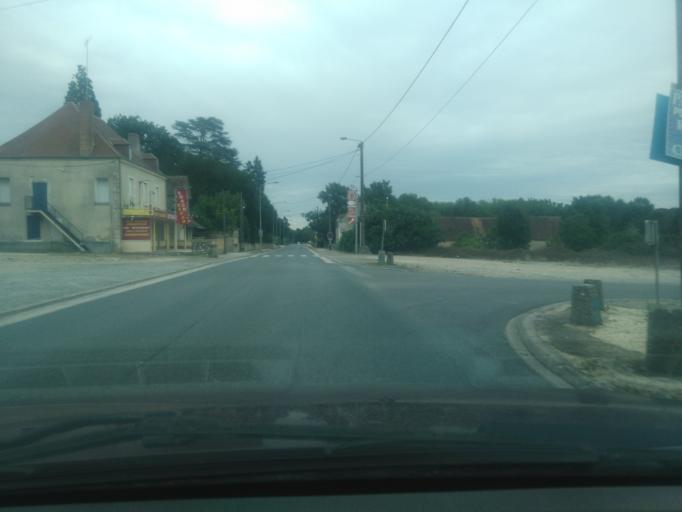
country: FR
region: Centre
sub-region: Departement de l'Indre
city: Saint-Gaultier
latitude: 46.6354
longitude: 1.2883
